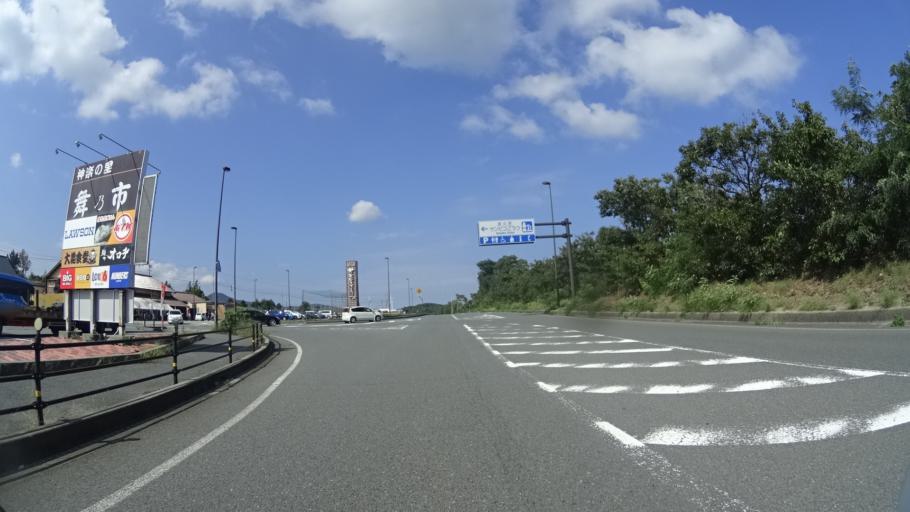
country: JP
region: Shimane
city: Gotsucho
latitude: 35.0458
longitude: 132.3000
